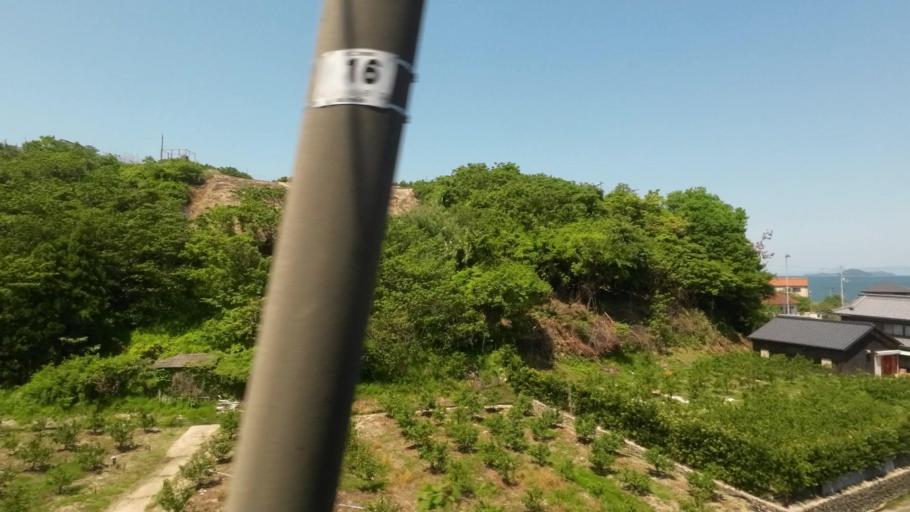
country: JP
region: Ehime
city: Hojo
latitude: 33.9990
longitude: 132.7753
